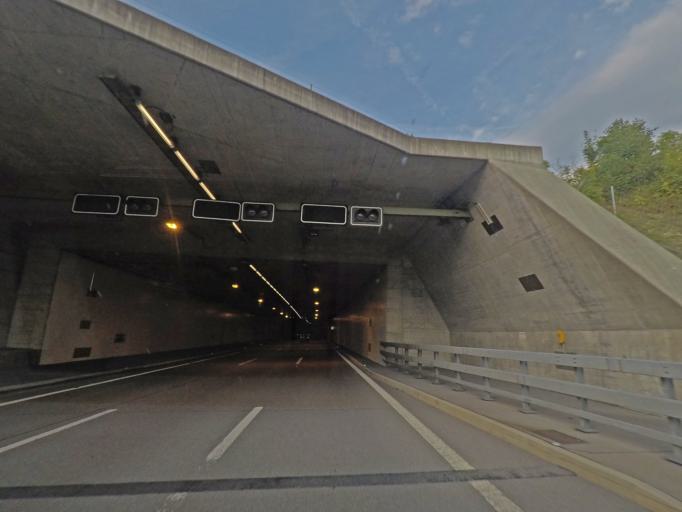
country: CH
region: Zurich
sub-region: Bezirk Affoltern
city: Wettswil / Wettswil (Dorf)
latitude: 47.3445
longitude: 8.4611
